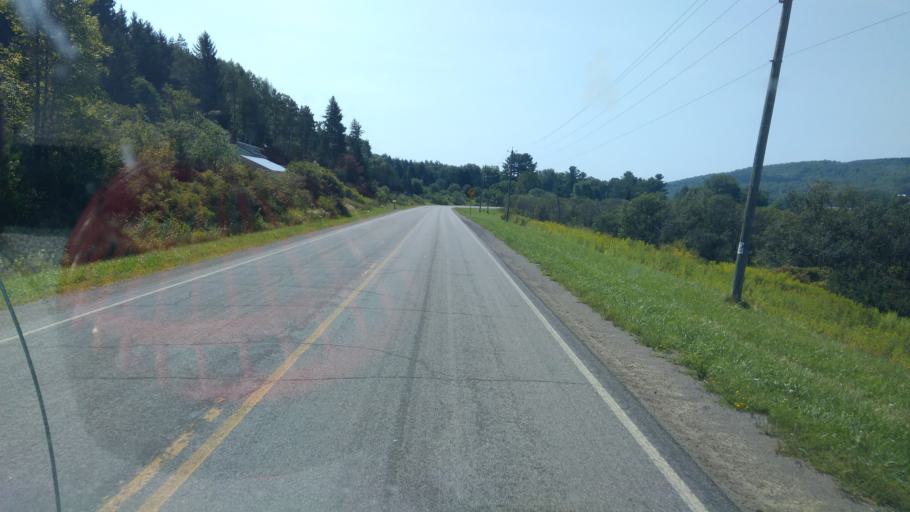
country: US
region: New York
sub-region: Allegany County
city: Belmont
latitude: 42.3244
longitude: -77.9389
